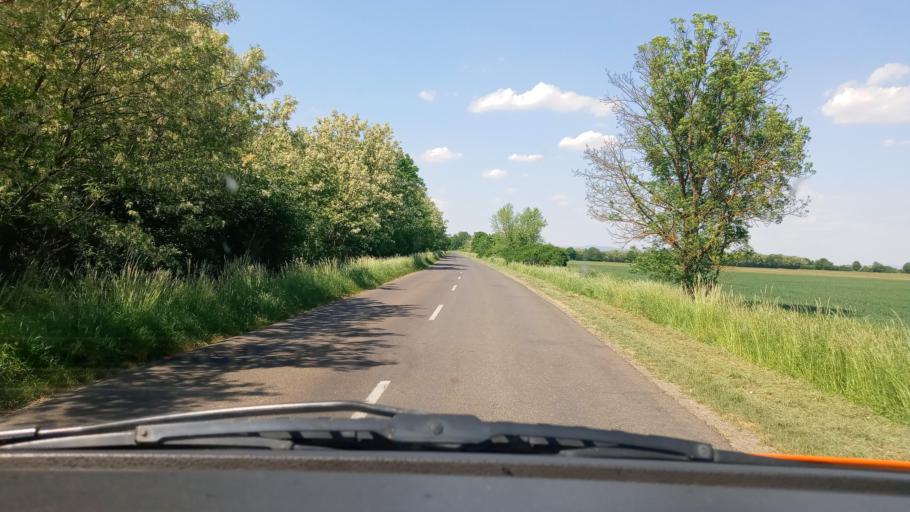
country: HU
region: Baranya
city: Harkany
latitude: 45.8871
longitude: 18.1721
